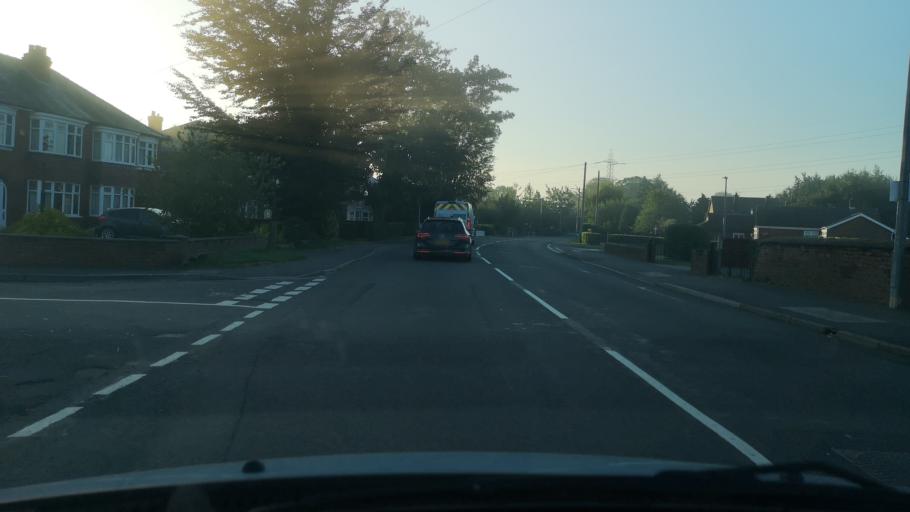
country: GB
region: England
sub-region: North Lincolnshire
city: Crowle
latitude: 53.6023
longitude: -0.8298
